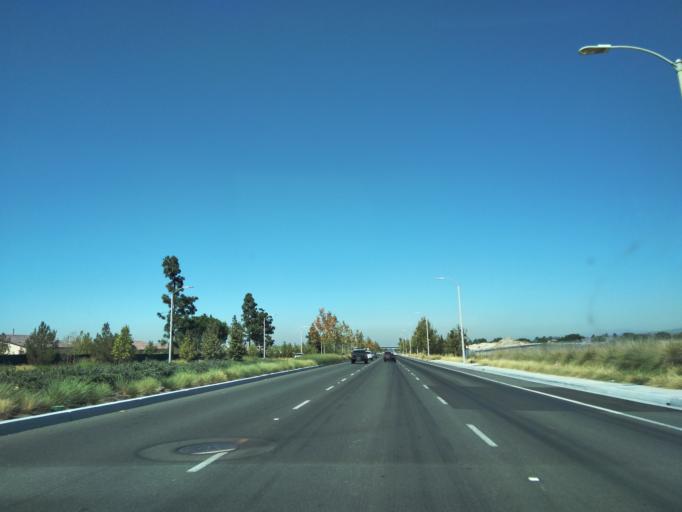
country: US
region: California
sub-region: Orange County
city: Lake Forest
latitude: 33.6907
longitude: -117.7268
